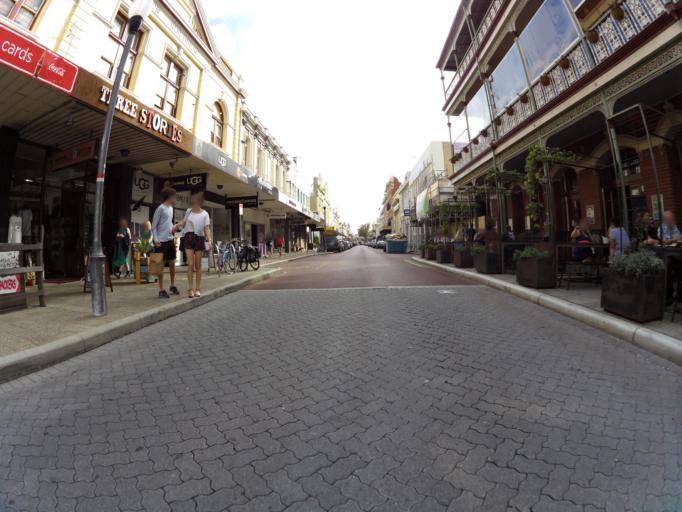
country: AU
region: Western Australia
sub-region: Fremantle
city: South Fremantle
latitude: -32.0545
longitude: 115.7462
